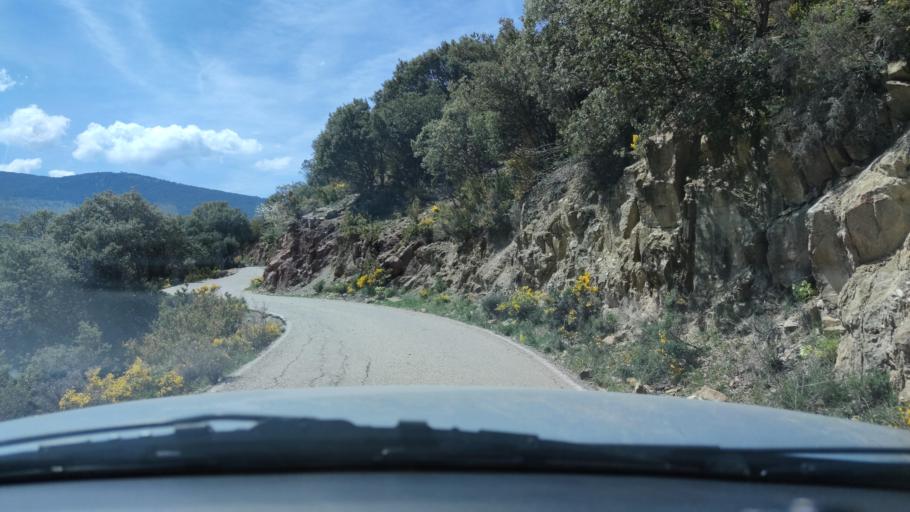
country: ES
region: Catalonia
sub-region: Provincia de Lleida
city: Sort
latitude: 42.3077
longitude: 1.1192
